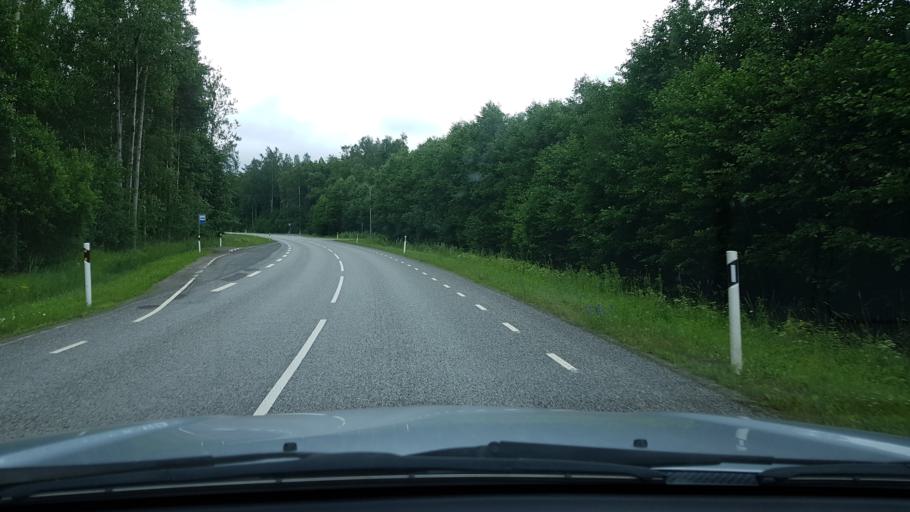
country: EE
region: Ida-Virumaa
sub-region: Narva-Joesuu linn
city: Narva-Joesuu
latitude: 59.3588
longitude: 27.9279
